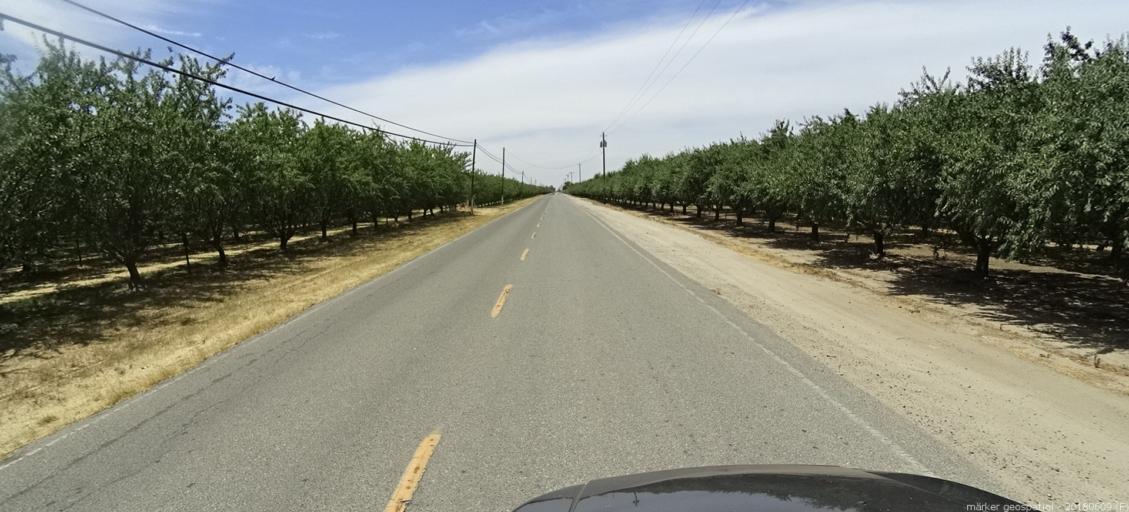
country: US
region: California
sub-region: Madera County
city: Parkwood
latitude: 36.9093
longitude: -120.0793
